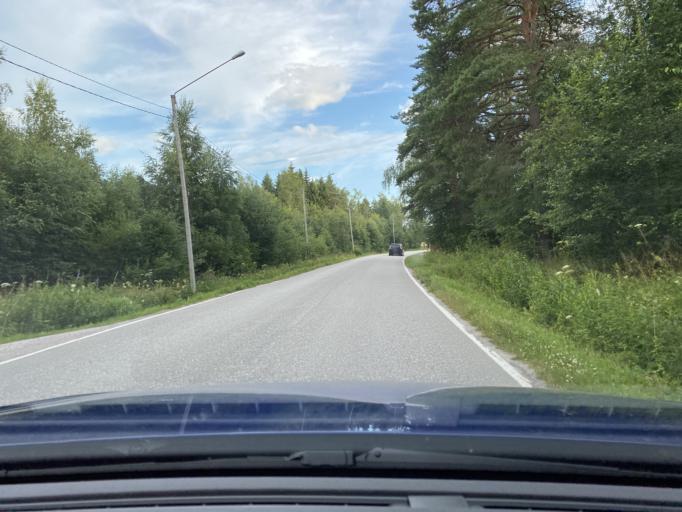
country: FI
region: Ostrobothnia
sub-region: Vaasa
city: Korsnaes
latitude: 62.9596
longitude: 21.1877
